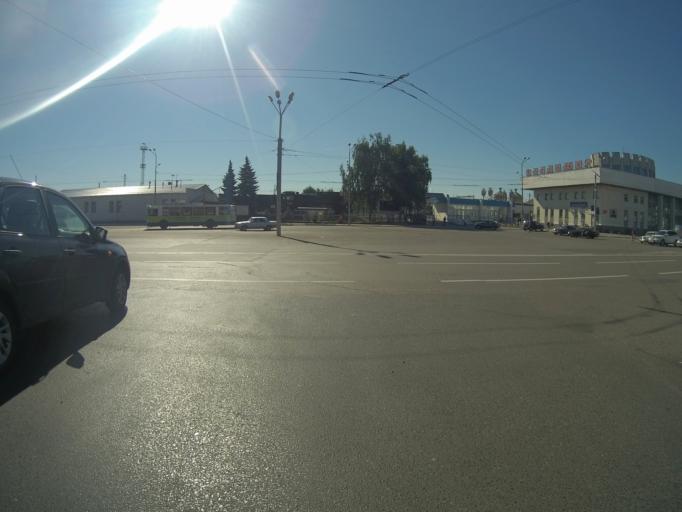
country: RU
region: Vladimir
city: Vladimir
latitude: 56.1311
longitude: 40.4208
